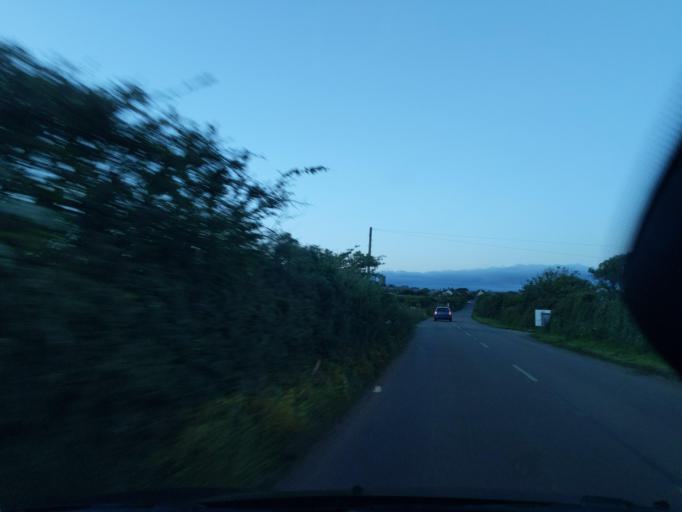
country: GB
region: England
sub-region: Cornwall
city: St. Buryan
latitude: 50.0695
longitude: -5.6308
